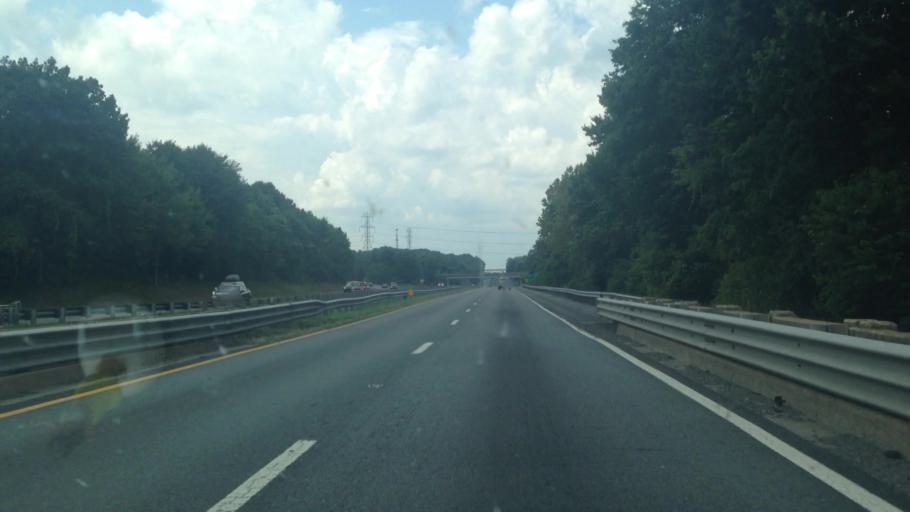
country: US
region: North Carolina
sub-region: Forsyth County
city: Tobaccoville
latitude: 36.2447
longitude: -80.3492
